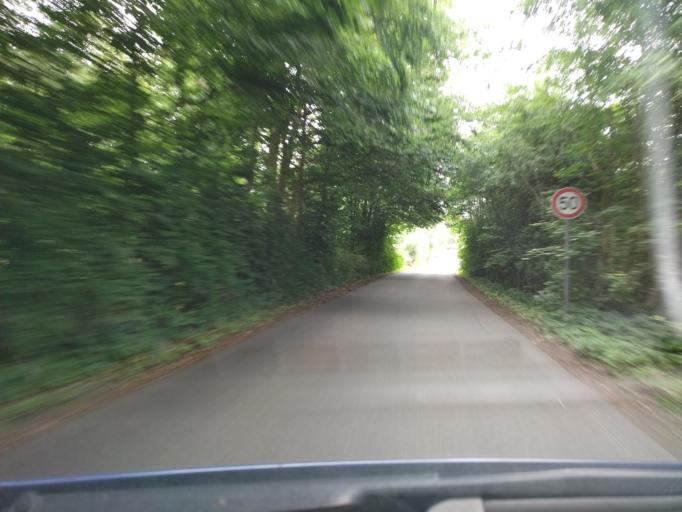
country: DE
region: Schleswig-Holstein
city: Schuby
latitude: 54.5150
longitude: 9.5174
